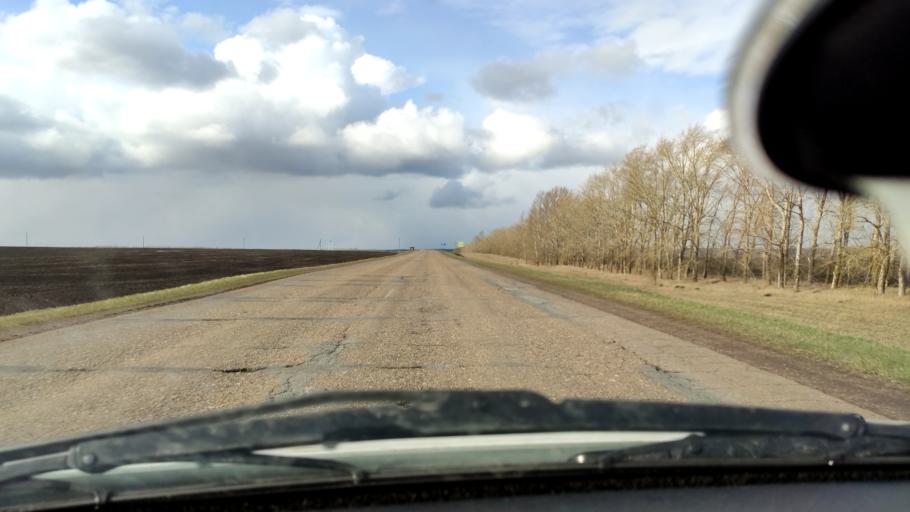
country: RU
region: Bashkortostan
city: Buzdyak
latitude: 54.7536
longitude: 54.5638
